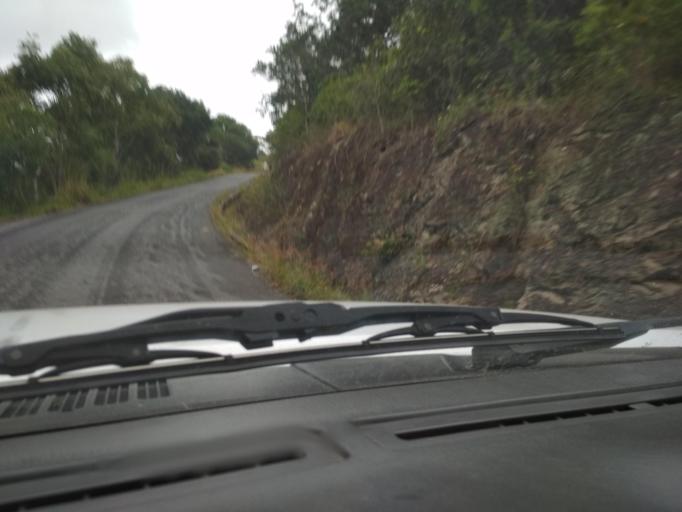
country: MX
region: Veracruz
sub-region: Emiliano Zapata
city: Dos Rios
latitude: 19.5264
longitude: -96.7979
